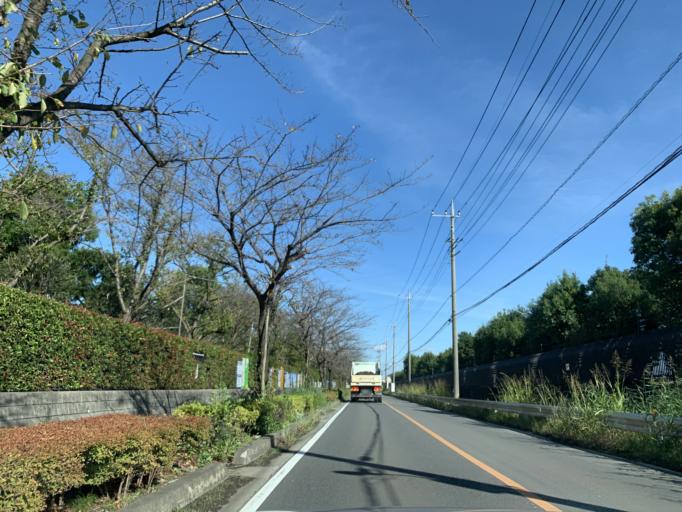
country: JP
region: Saitama
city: Yashio-shi
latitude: 35.8342
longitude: 139.8703
